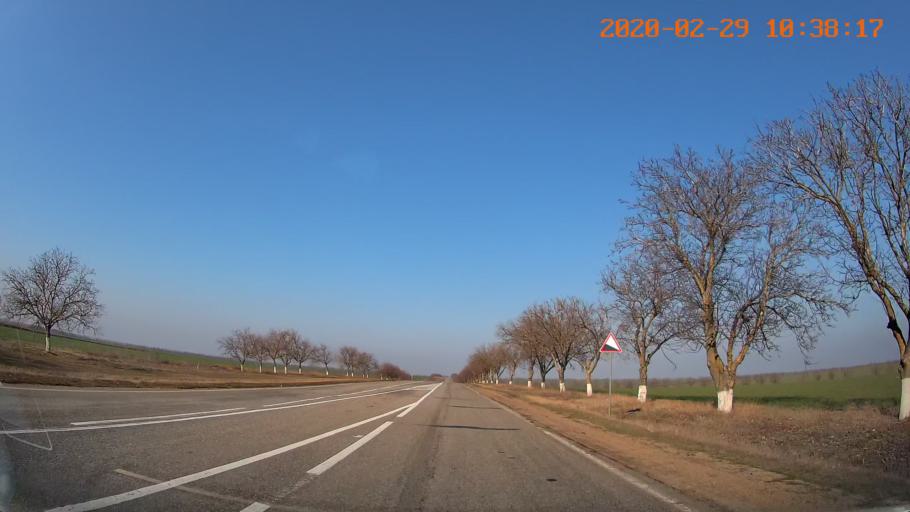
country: MD
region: Anenii Noi
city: Varnita
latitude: 47.0150
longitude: 29.4760
